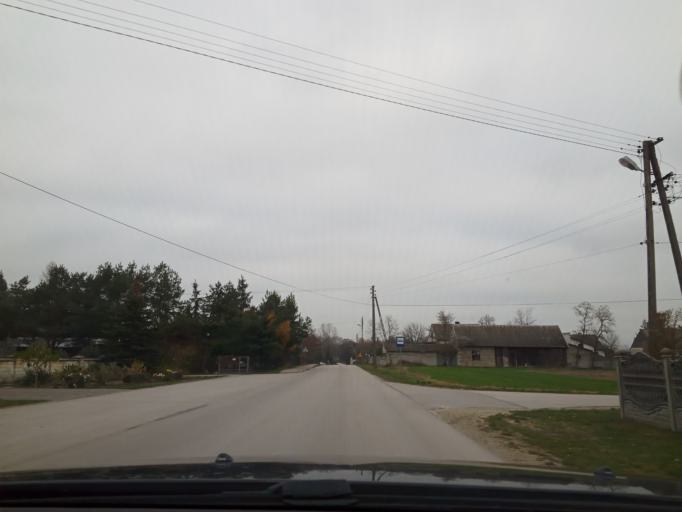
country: PL
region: Swietokrzyskie
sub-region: Powiat jedrzejowski
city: Imielno
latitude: 50.6005
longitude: 20.4856
